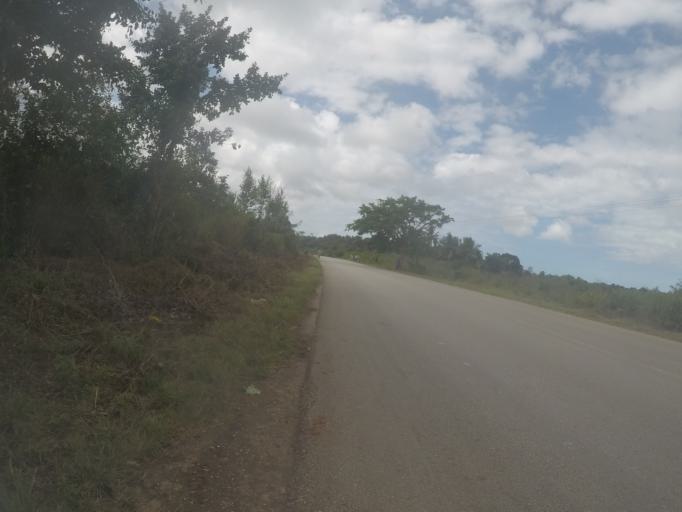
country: TZ
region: Zanzibar North
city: Kijini
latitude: -5.8347
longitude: 39.2901
